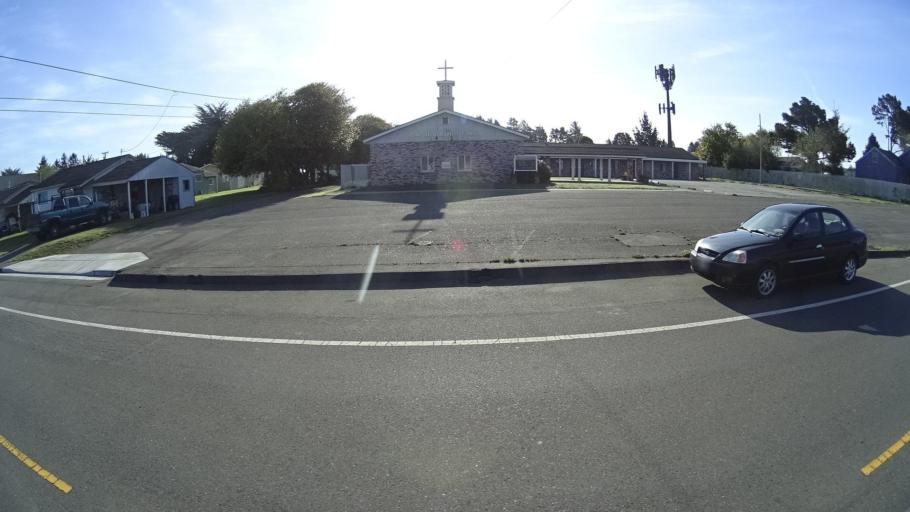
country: US
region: California
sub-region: Humboldt County
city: Bayview
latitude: 40.7654
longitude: -124.1756
